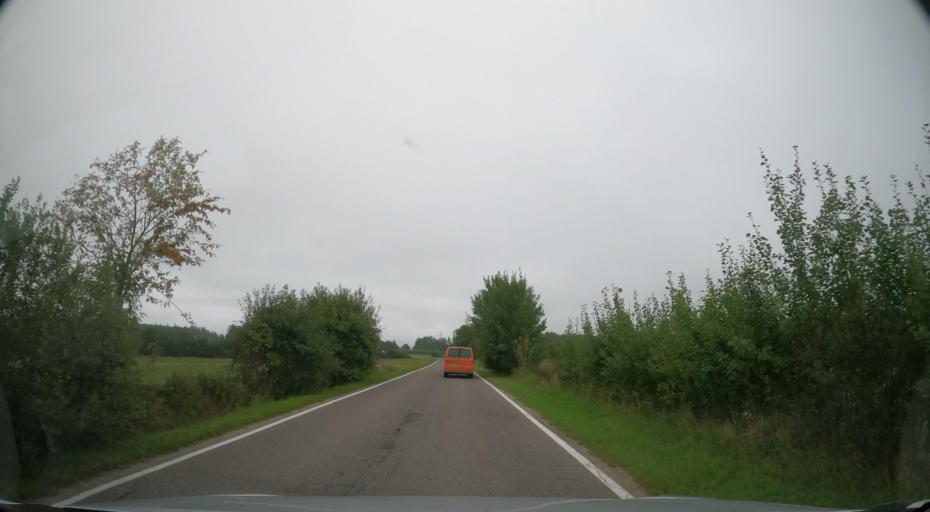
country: PL
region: Pomeranian Voivodeship
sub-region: Powiat wejherowski
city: Szemud
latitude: 54.5022
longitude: 18.1633
